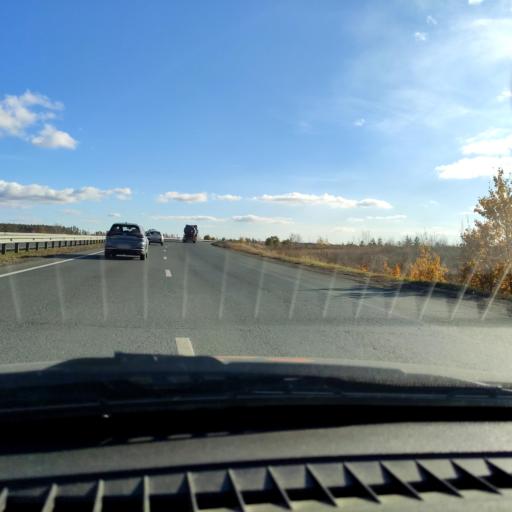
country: RU
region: Samara
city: Zhigulevsk
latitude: 53.5163
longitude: 49.5361
